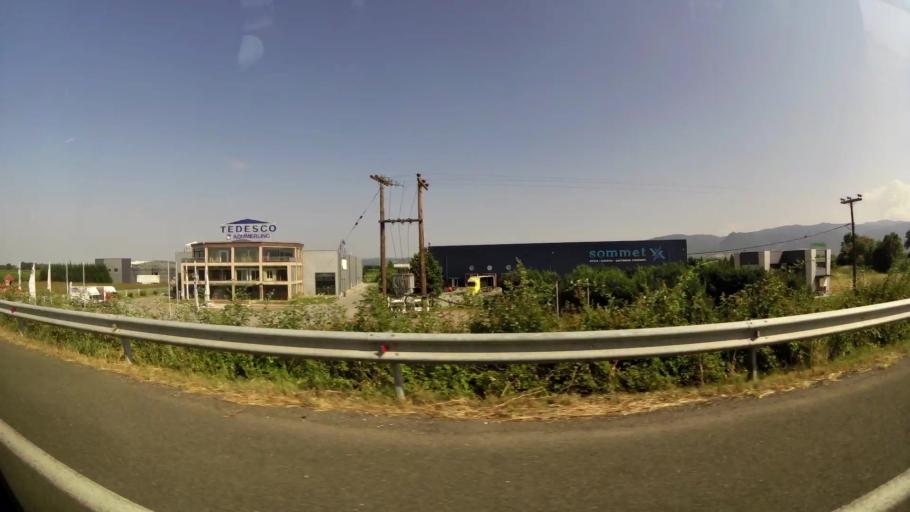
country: GR
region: Central Macedonia
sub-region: Nomos Imathias
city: Kouloura
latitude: 40.5450
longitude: 22.3250
